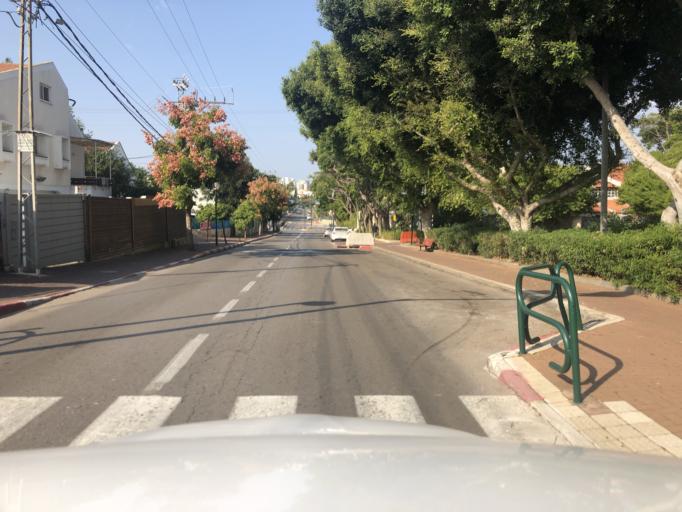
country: IL
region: Central District
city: Kfar Saba
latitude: 32.1841
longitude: 34.9090
